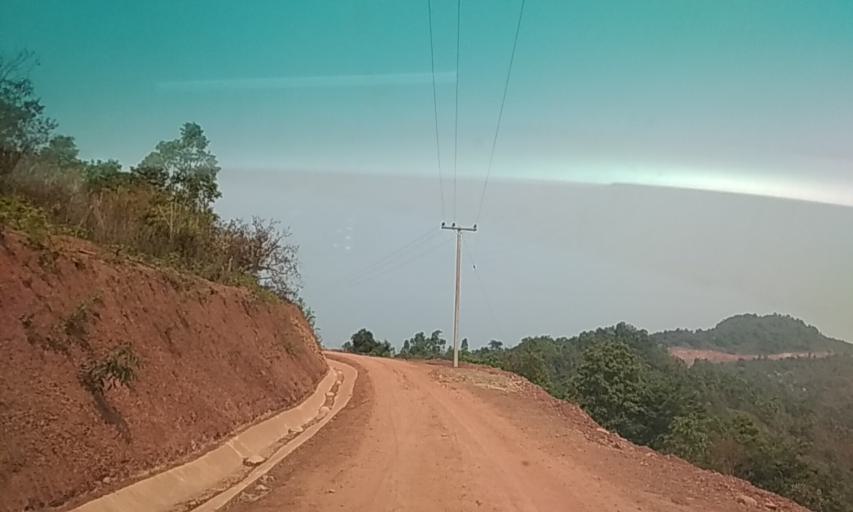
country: VN
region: Huyen Dien Bien
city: Dien Bien Phu
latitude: 21.4646
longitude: 102.7724
